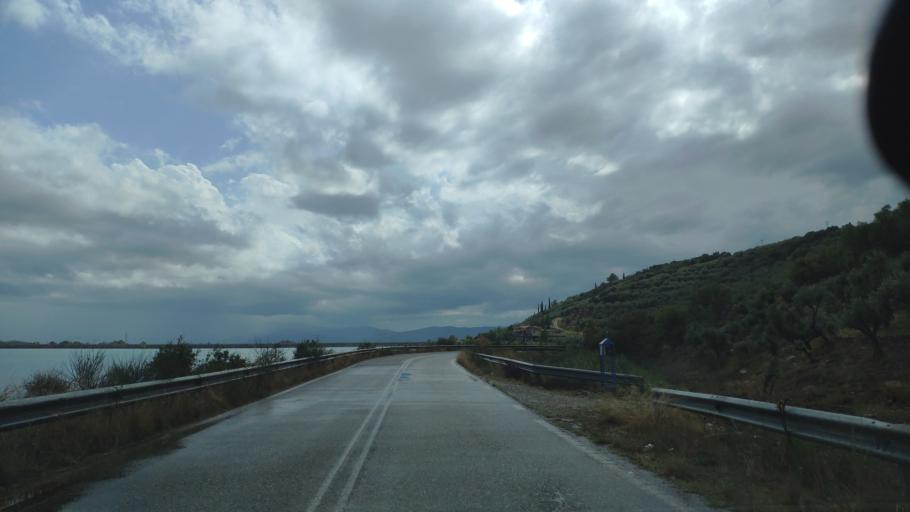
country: GR
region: West Greece
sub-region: Nomos Aitolias kai Akarnanias
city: Lepenou
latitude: 38.6862
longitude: 21.3233
